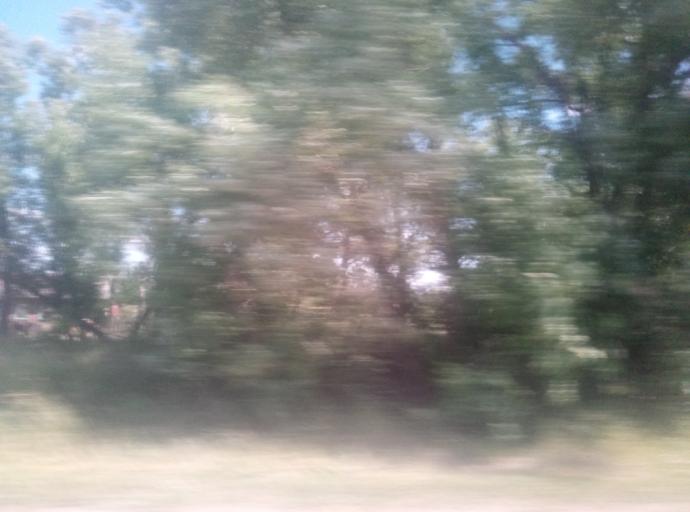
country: RU
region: Tula
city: Kireyevsk
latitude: 53.9636
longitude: 37.9371
